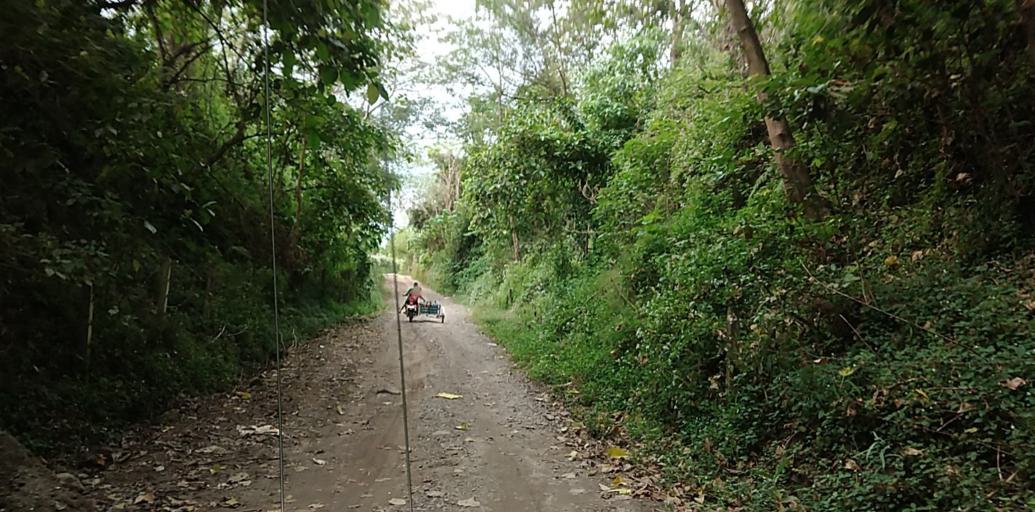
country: PH
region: Central Luzon
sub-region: Province of Pampanga
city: Babo-Pangulo
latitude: 15.1111
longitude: 120.4969
